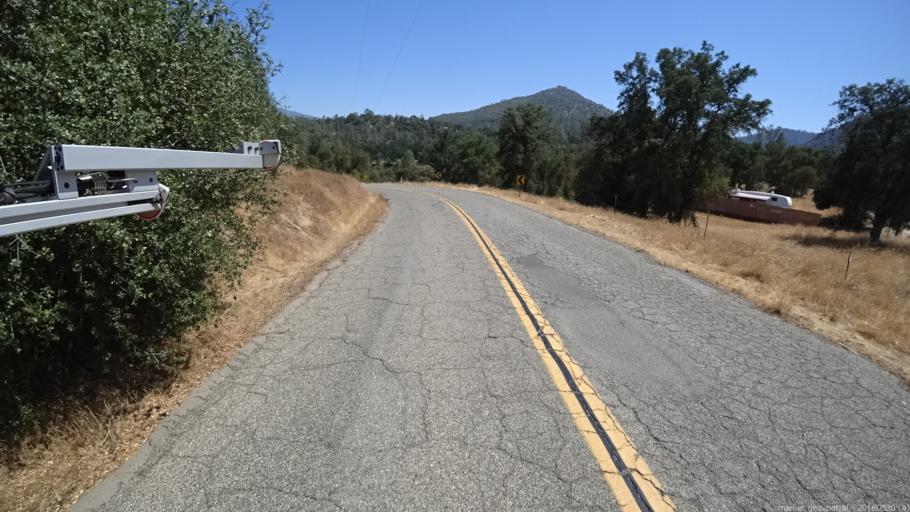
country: US
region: California
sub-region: Fresno County
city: Auberry
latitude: 37.1516
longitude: -119.5120
